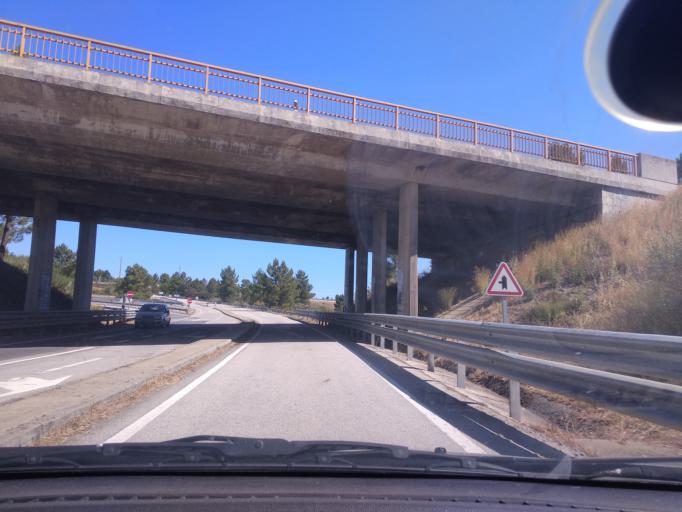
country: PT
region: Castelo Branco
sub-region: Castelo Branco
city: Castelo Branco
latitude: 39.7511
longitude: -7.6204
